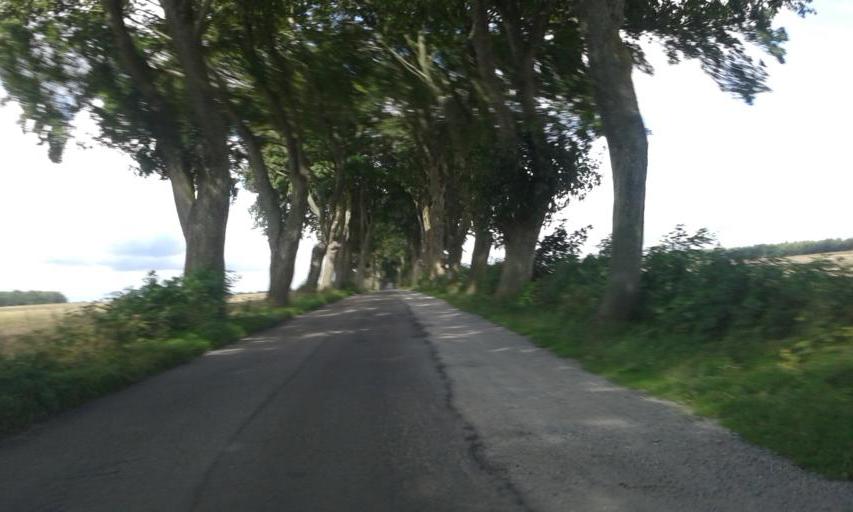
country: PL
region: West Pomeranian Voivodeship
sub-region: Powiat slawienski
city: Slawno
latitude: 54.3129
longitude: 16.6115
